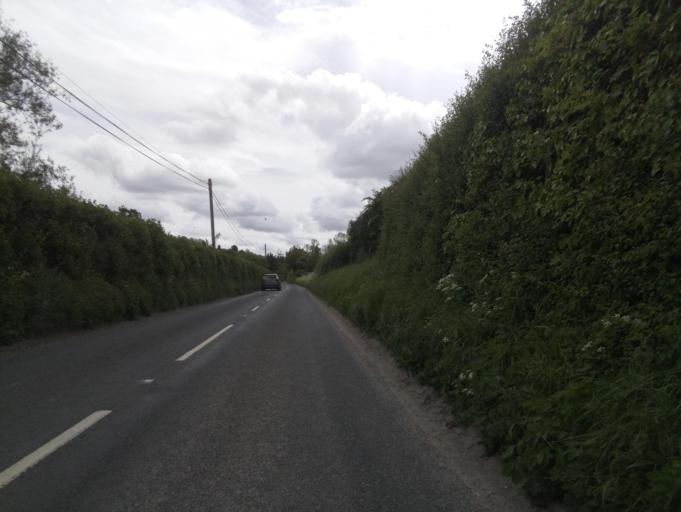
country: GB
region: England
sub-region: Dorset
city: Dorchester
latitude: 50.7489
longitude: -2.4670
